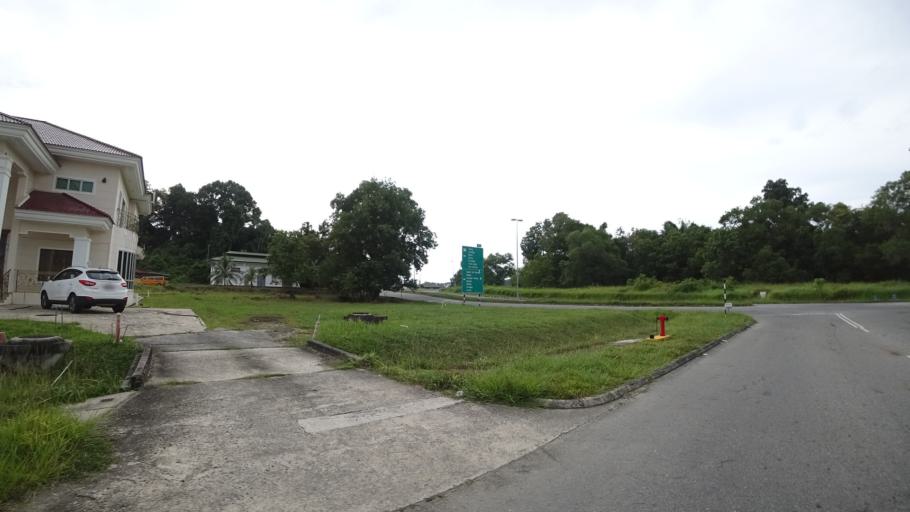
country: BN
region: Brunei and Muara
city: Bandar Seri Begawan
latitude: 4.9805
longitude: 114.9596
